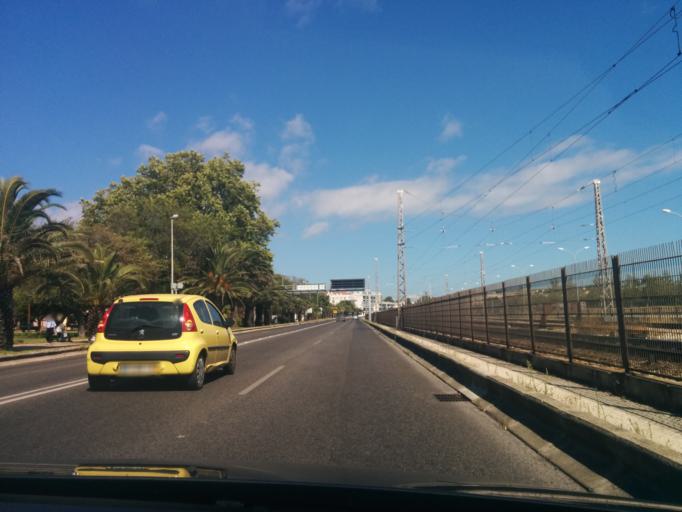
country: PT
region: Lisbon
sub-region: Oeiras
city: Alges
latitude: 38.6987
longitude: -9.2341
